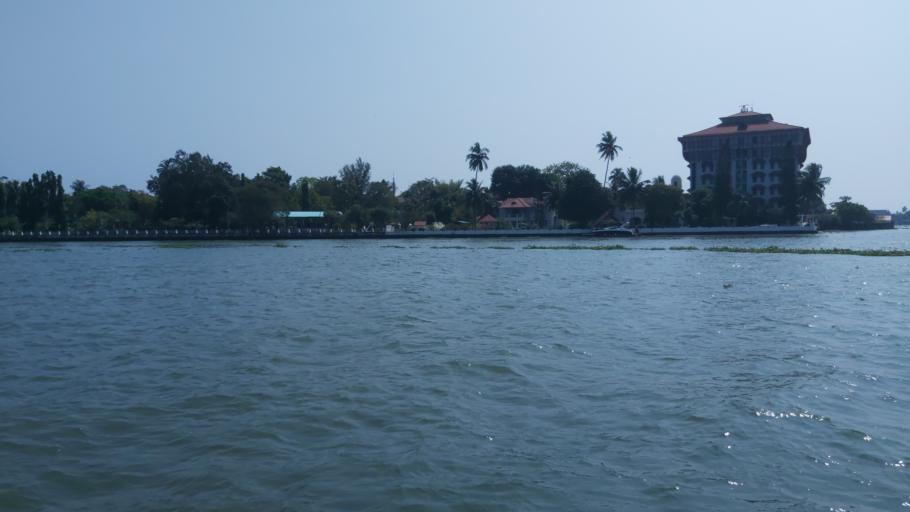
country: IN
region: Kerala
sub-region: Ernakulam
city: Cochin
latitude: 9.9721
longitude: 76.2598
